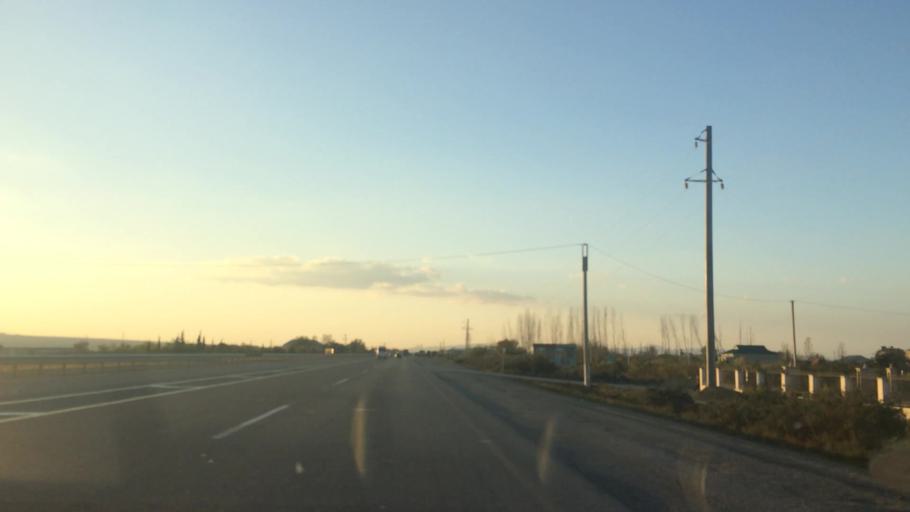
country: AZ
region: Haciqabul
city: Haciqabul
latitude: 40.0077
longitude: 49.1572
